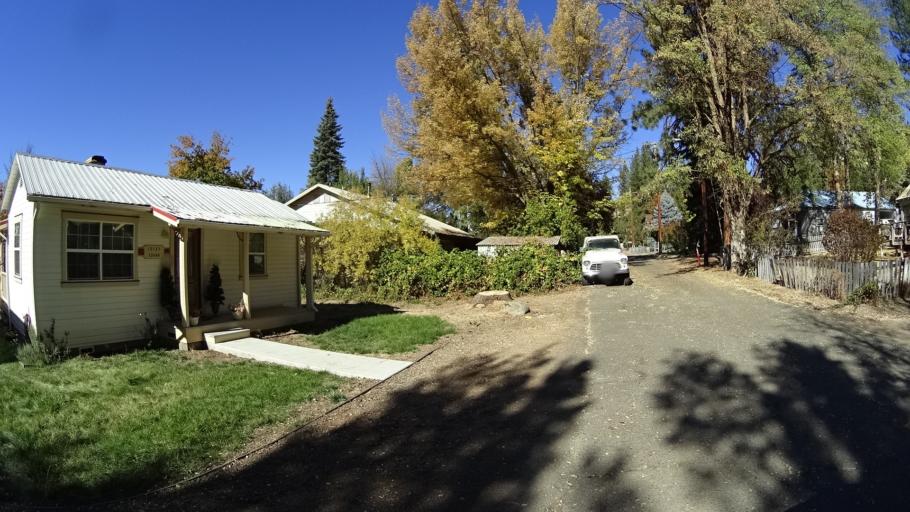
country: US
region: California
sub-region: Siskiyou County
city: Yreka
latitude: 41.6106
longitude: -122.8379
